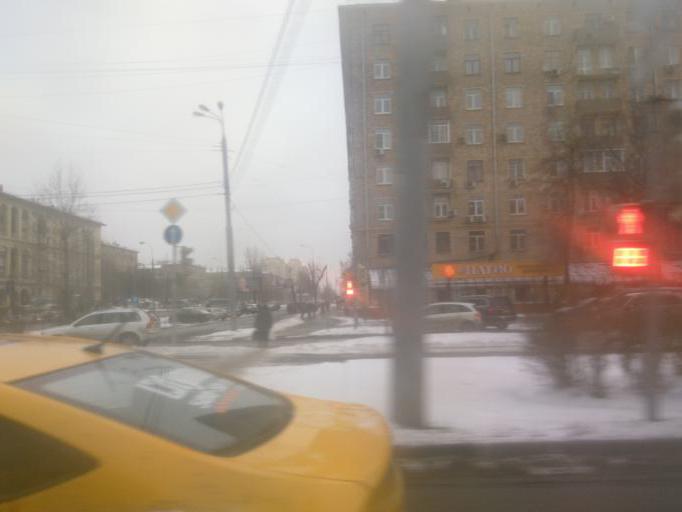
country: RU
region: Moskovskaya
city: Semenovskoye
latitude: 55.6884
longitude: 37.5457
